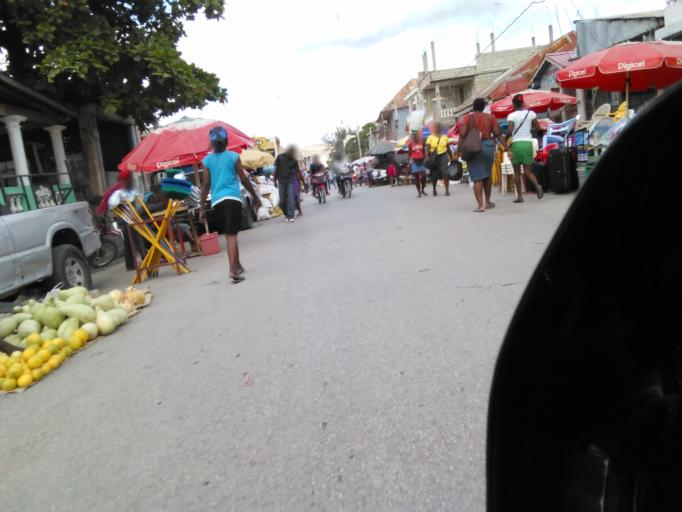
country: HT
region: Artibonite
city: Saint-Marc
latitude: 19.1069
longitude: -72.7001
